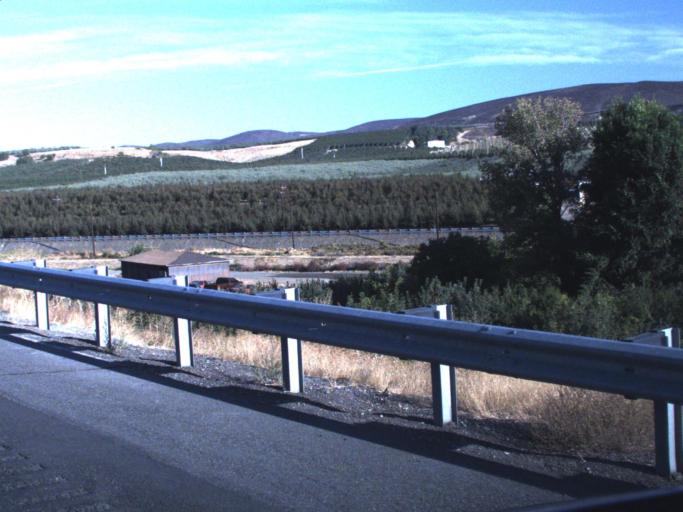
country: US
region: Washington
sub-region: Yakima County
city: Wapato
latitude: 46.4950
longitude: -120.4358
